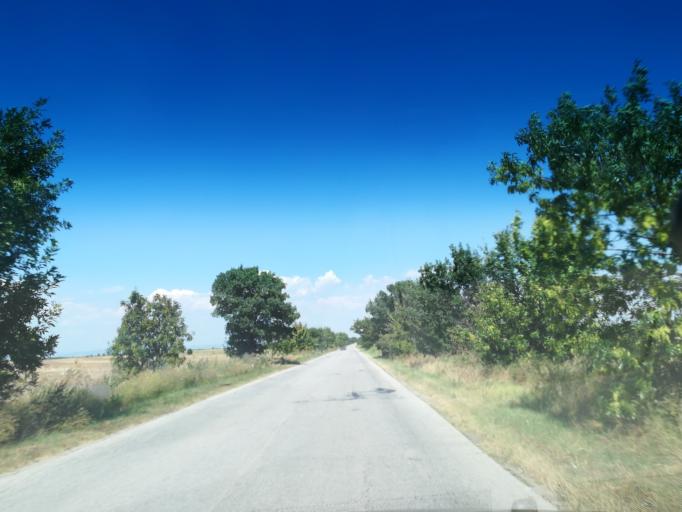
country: BG
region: Plovdiv
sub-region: Obshtina Sadovo
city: Sadovo
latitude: 42.0464
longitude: 25.1406
